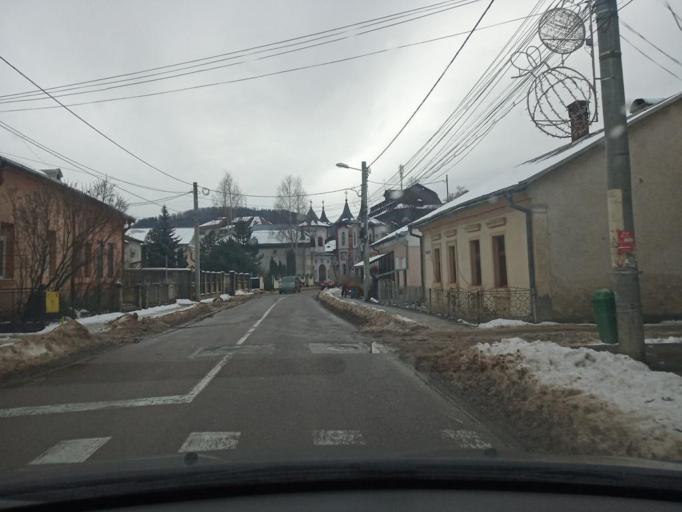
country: RO
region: Suceava
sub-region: Oras Gura Humorului
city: Gura Humorului
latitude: 47.5569
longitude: 25.8904
